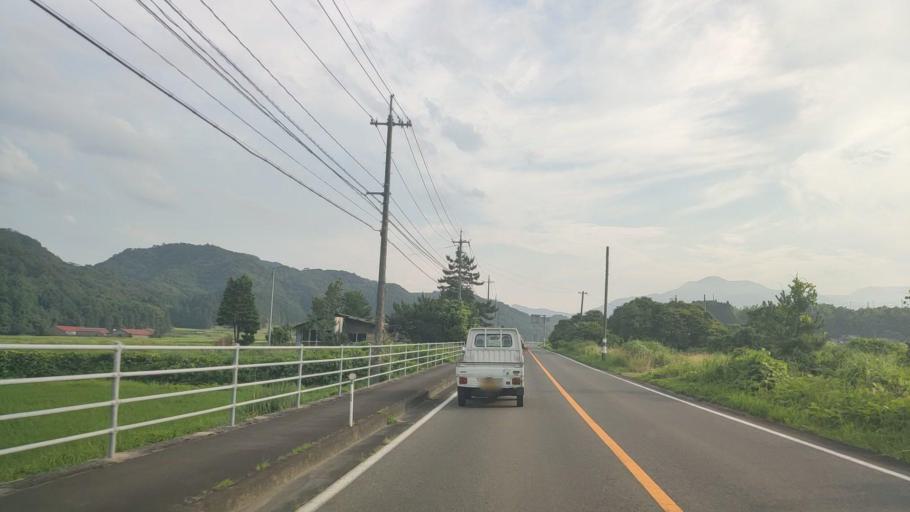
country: JP
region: Tottori
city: Kurayoshi
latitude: 35.3813
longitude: 133.7769
